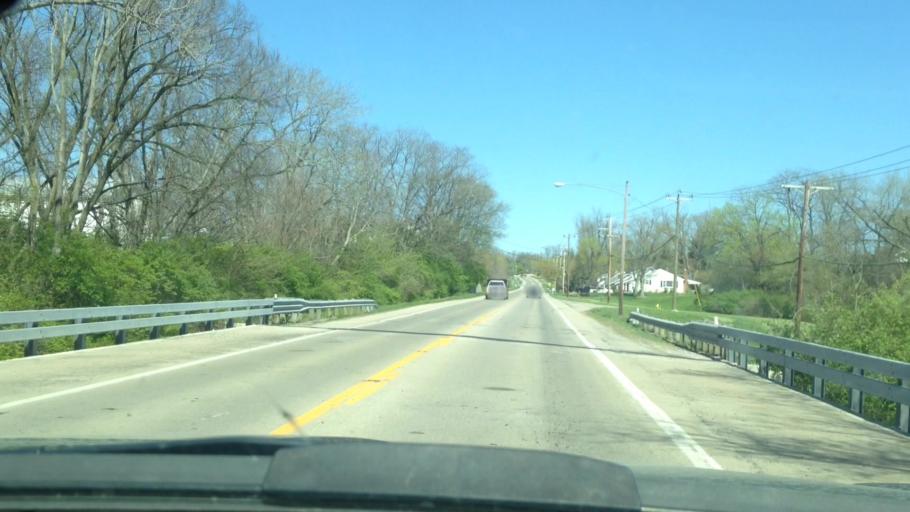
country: US
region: Ohio
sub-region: Butler County
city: Ross
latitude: 39.3921
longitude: -84.6514
